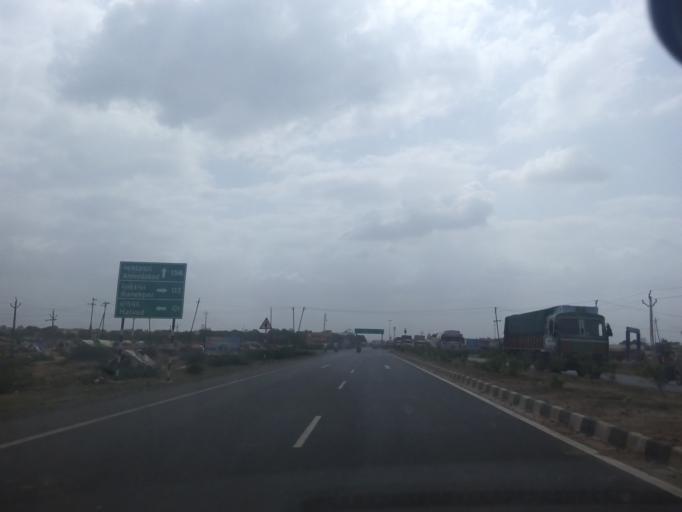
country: IN
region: Gujarat
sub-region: Surendranagar
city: Halvad
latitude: 23.0036
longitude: 71.1795
